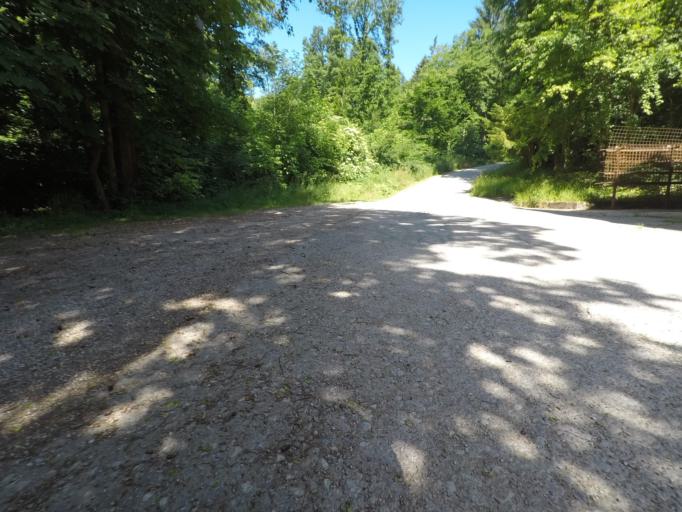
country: AT
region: Lower Austria
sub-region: Politischer Bezirk Modling
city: Perchtoldsdorf
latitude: 48.1726
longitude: 16.2438
